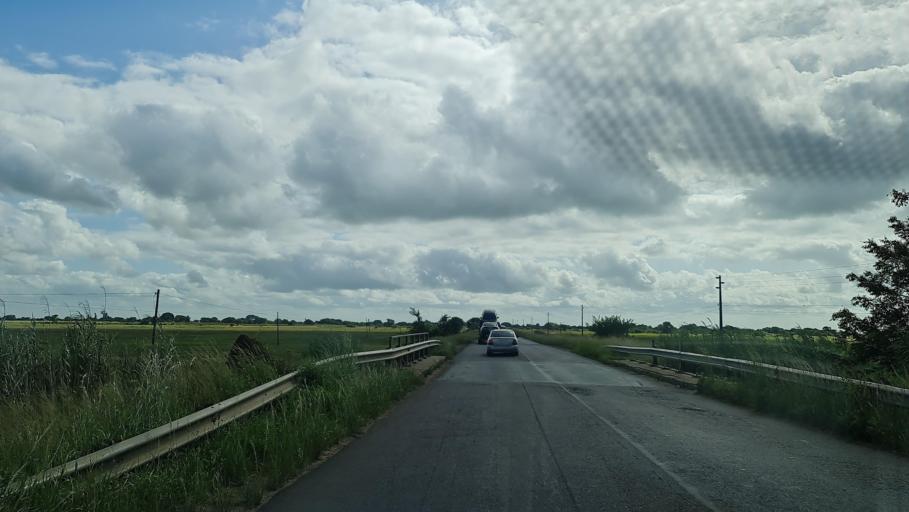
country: MZ
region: Gaza
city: Macia
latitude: -25.0946
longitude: 32.8334
